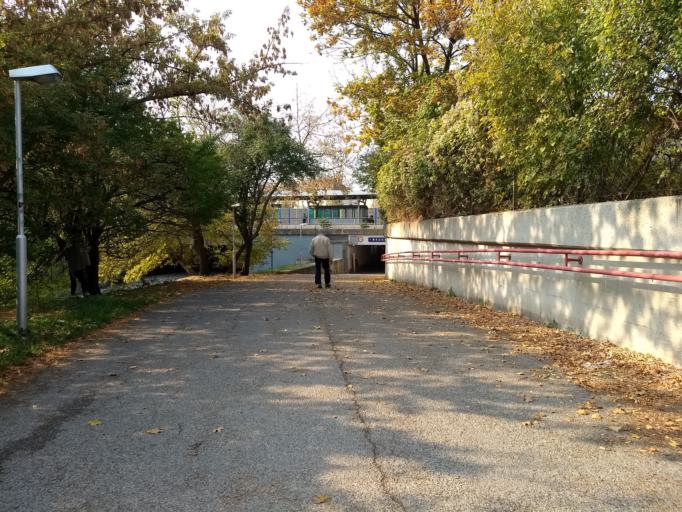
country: AT
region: Lower Austria
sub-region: Politischer Bezirk Modling
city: Perchtoldsdorf
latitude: 48.1347
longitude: 16.2852
